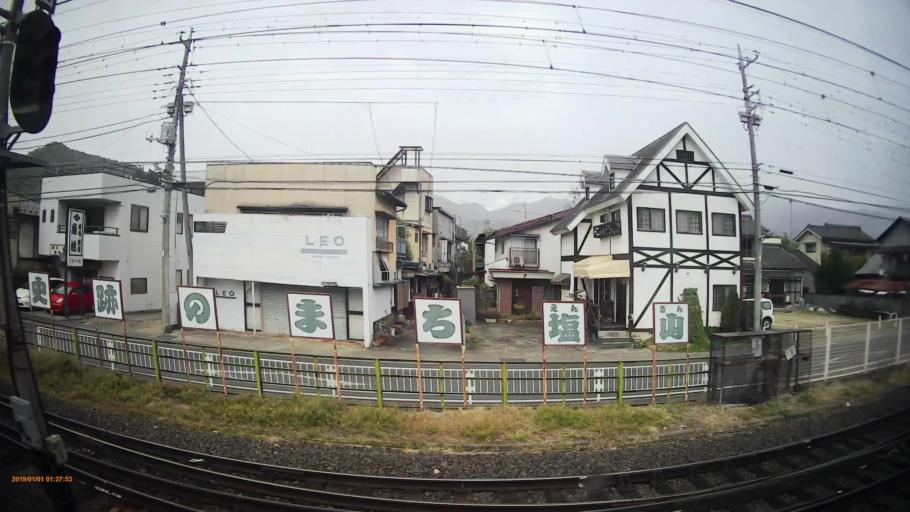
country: JP
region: Yamanashi
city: Enzan
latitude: 35.7057
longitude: 138.7320
